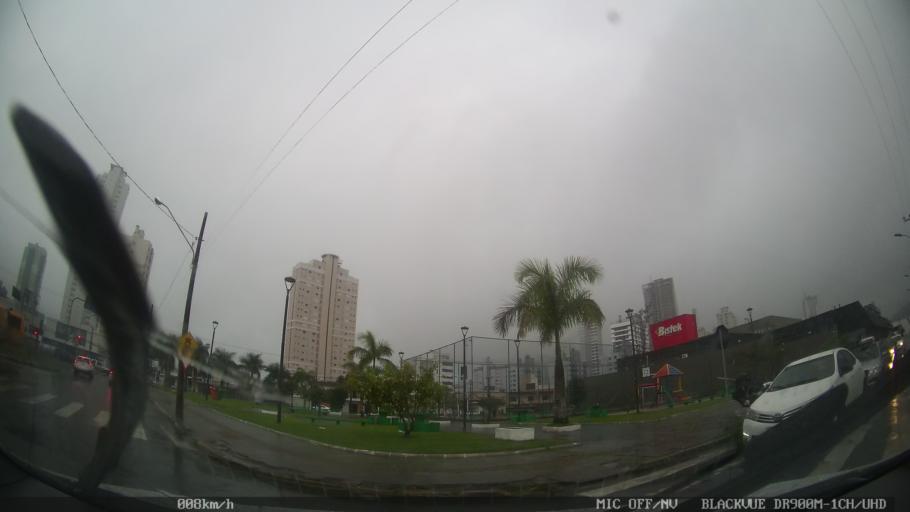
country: BR
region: Santa Catarina
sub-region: Itajai
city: Itajai
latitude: -26.9178
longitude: -48.6558
